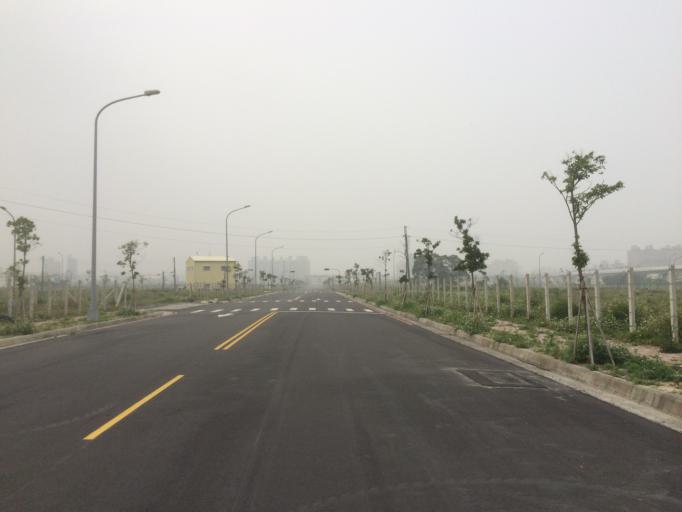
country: TW
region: Taiwan
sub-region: Taichung City
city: Taichung
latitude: 24.1797
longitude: 120.7039
